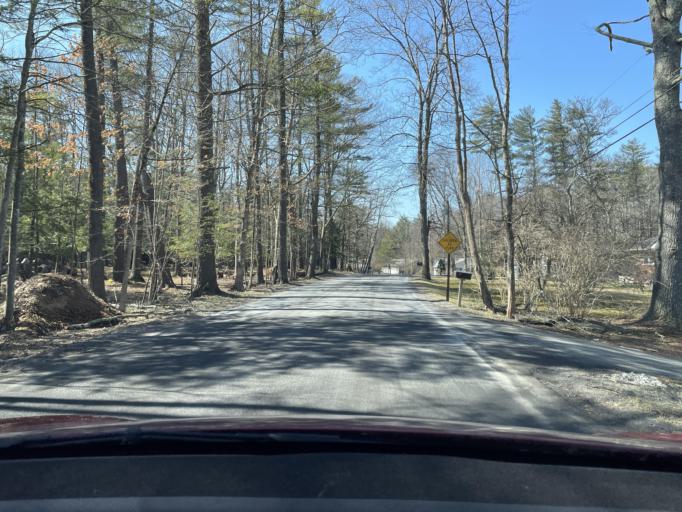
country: US
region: New York
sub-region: Ulster County
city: Woodstock
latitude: 42.0427
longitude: -74.1038
